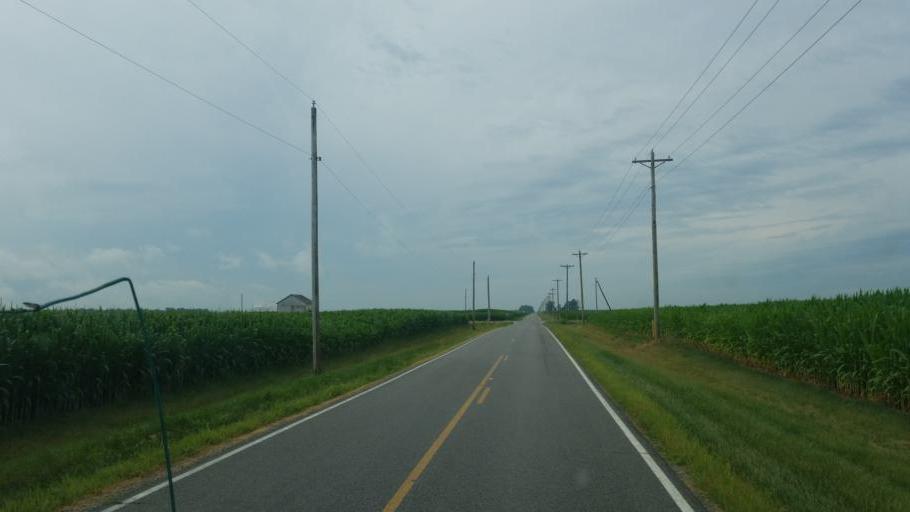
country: US
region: Ohio
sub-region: Defiance County
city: Hicksville
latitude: 41.3265
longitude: -84.6899
